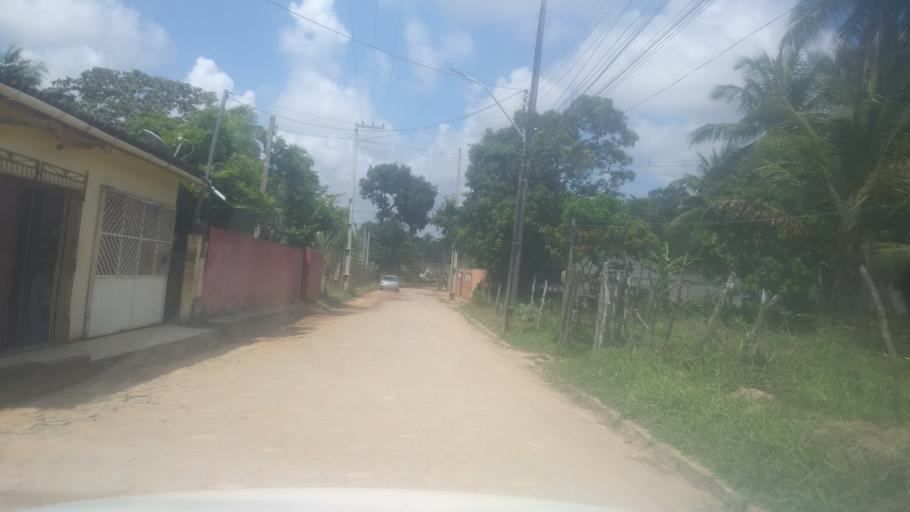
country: BR
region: Rio Grande do Norte
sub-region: Sao Jose De Mipibu
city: Sao Jose de Mipibu
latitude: -6.0713
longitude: -35.2277
